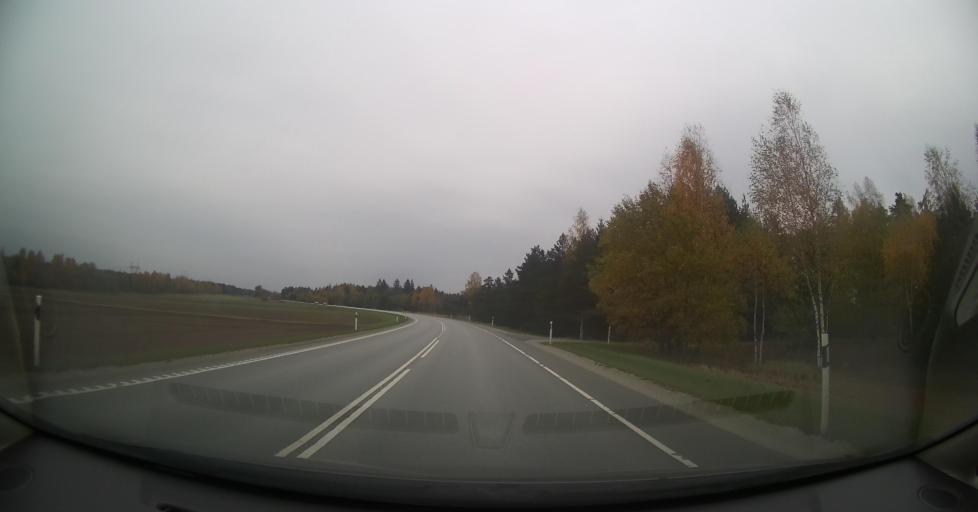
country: EE
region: Harju
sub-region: Nissi vald
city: Riisipere
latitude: 59.1318
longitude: 24.3184
